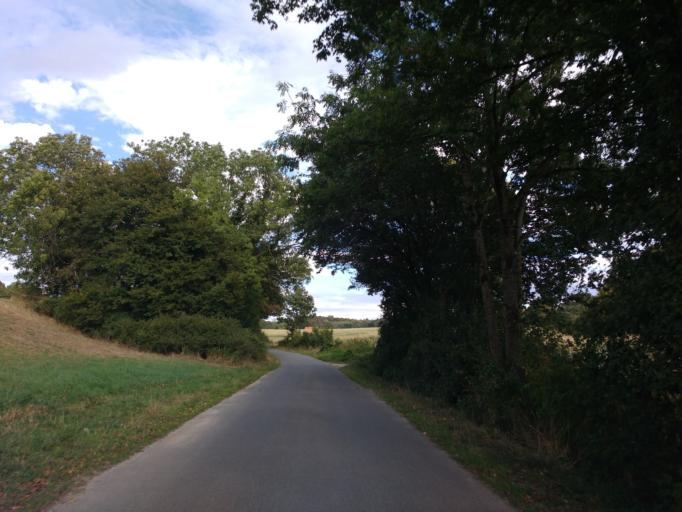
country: DE
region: North Rhine-Westphalia
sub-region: Regierungsbezirk Detmold
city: Schlangen
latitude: 51.7915
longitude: 8.8544
